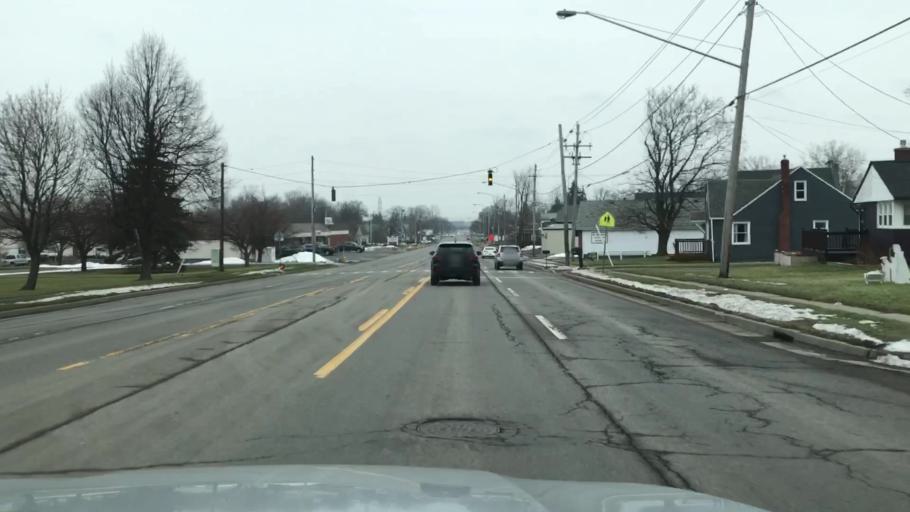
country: US
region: New York
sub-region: Erie County
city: Blasdell
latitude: 42.8000
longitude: -78.7959
